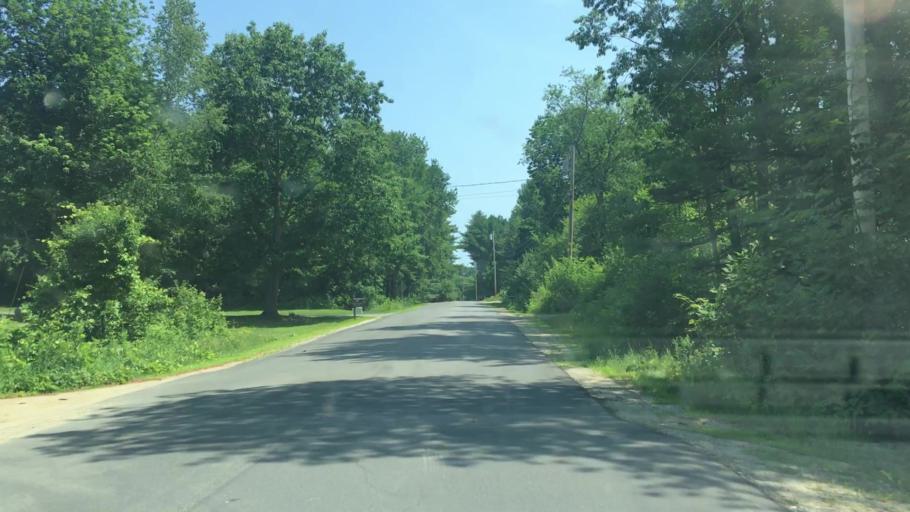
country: US
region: Maine
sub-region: Kennebec County
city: Monmouth
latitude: 44.2730
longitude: -70.0505
